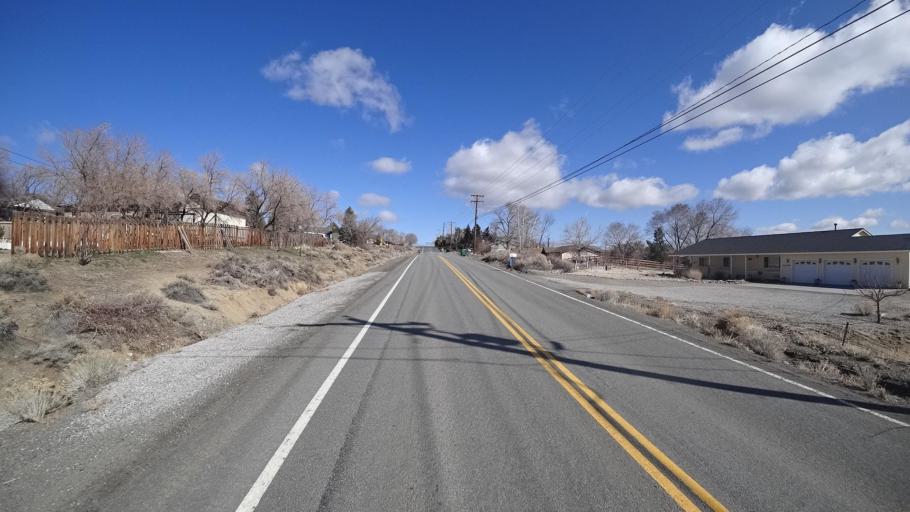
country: US
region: Nevada
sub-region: Washoe County
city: Cold Springs
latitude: 39.6615
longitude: -119.9225
